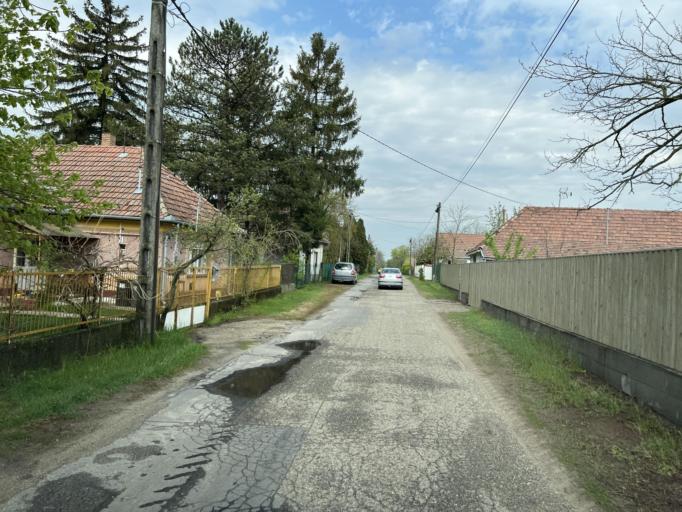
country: HU
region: Pest
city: Hernad
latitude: 47.1783
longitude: 19.4660
